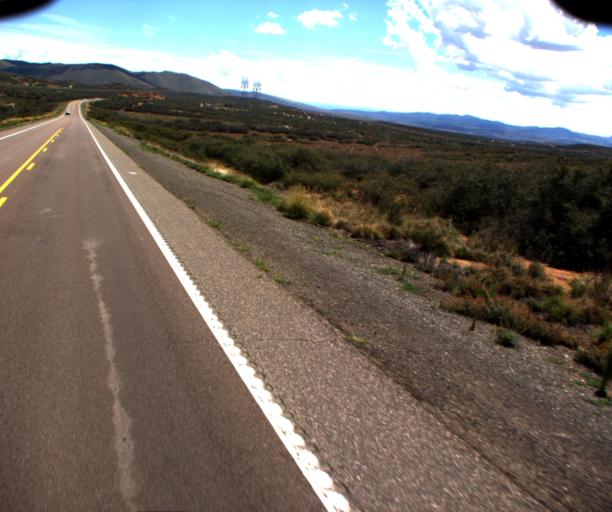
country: US
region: Arizona
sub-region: Yavapai County
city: Dewey-Humboldt
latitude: 34.5454
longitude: -112.1798
